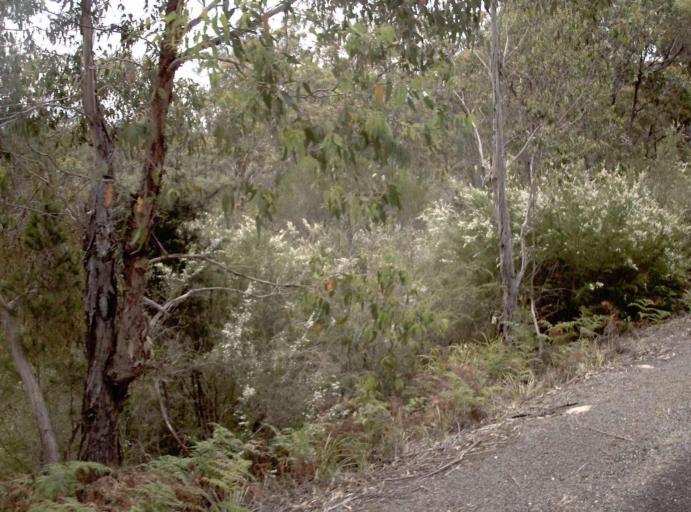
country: AU
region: New South Wales
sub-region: Bega Valley
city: Eden
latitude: -37.4867
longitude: 149.5502
